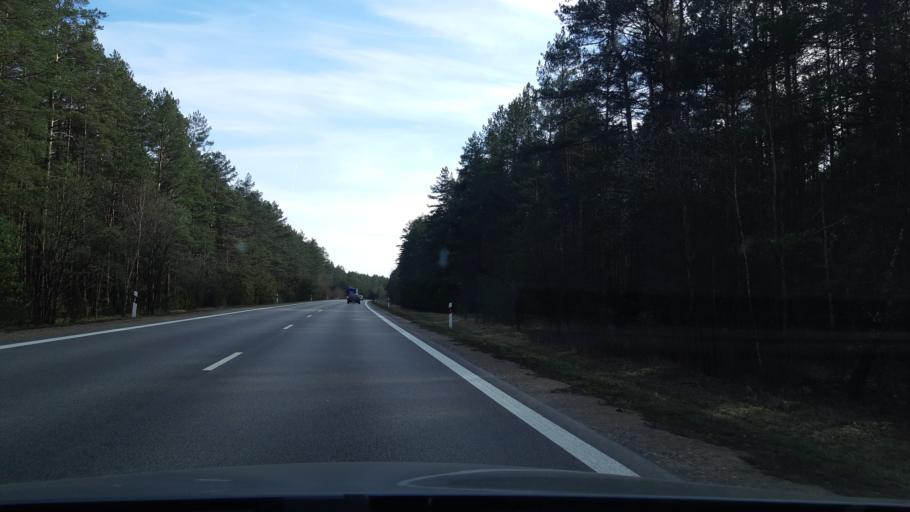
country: LT
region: Alytaus apskritis
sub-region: Alytaus rajonas
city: Daugai
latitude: 54.1288
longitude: 24.2107
